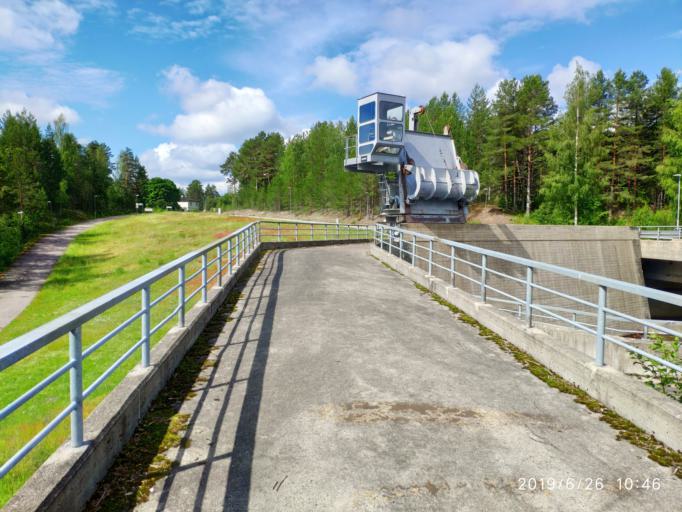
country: NO
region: Hedmark
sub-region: Elverum
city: Elverum
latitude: 60.8306
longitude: 11.6116
